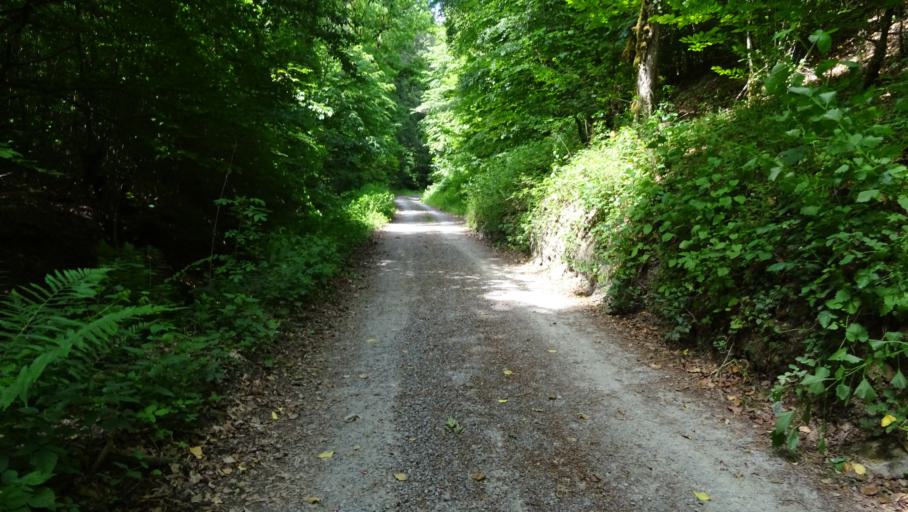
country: DE
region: Baden-Wuerttemberg
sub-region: Karlsruhe Region
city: Hassmersheim
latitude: 49.2964
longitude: 9.1585
